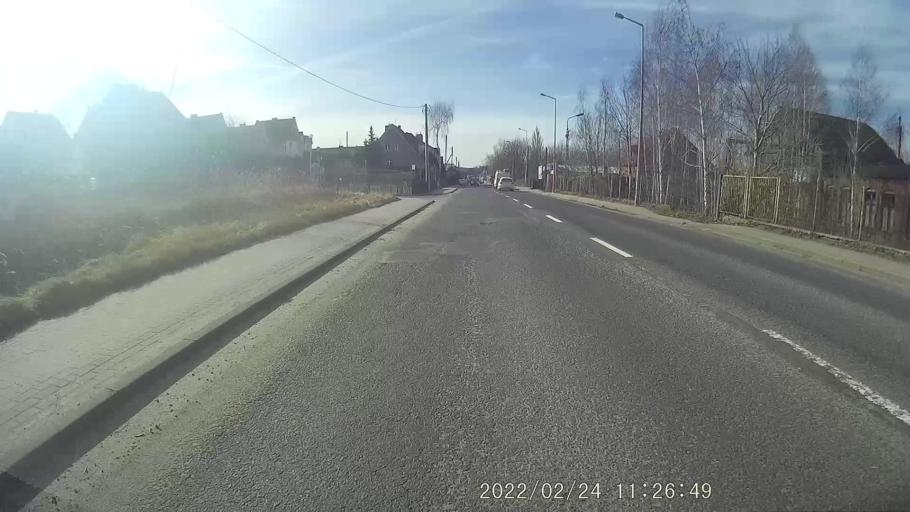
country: PL
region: Lubusz
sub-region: Powiat zaganski
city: Szprotawa
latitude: 51.5342
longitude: 15.6452
